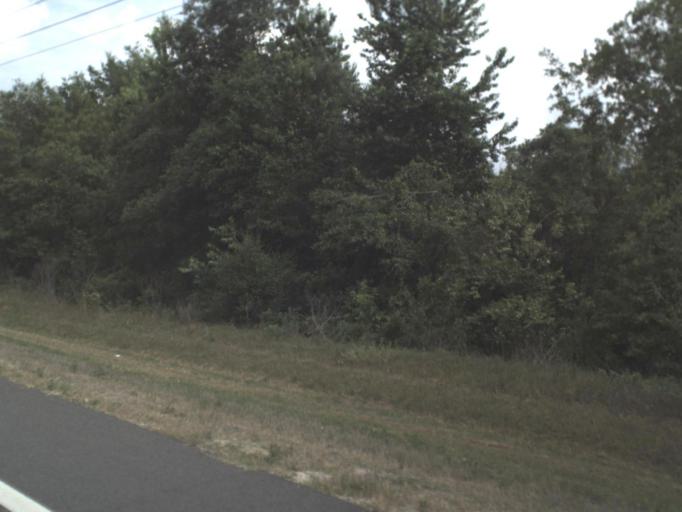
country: US
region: Florida
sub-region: Putnam County
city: Interlachen
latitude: 29.6229
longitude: -81.9381
